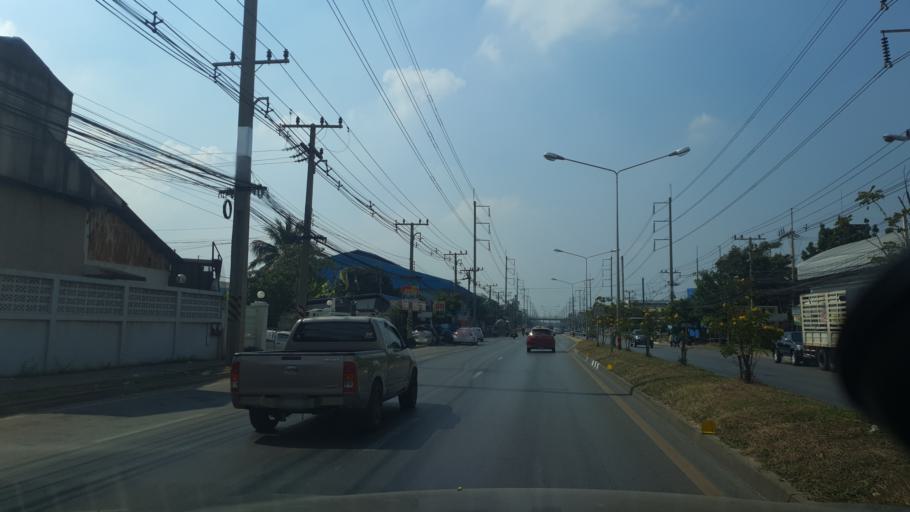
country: TH
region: Samut Sakhon
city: Krathum Baen
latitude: 13.6697
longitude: 100.2802
